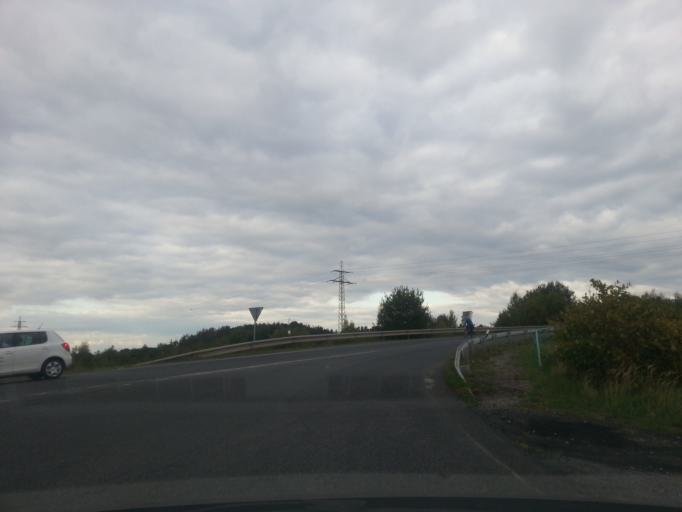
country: CZ
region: Central Bohemia
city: Unhost'
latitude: 50.1026
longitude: 14.1385
